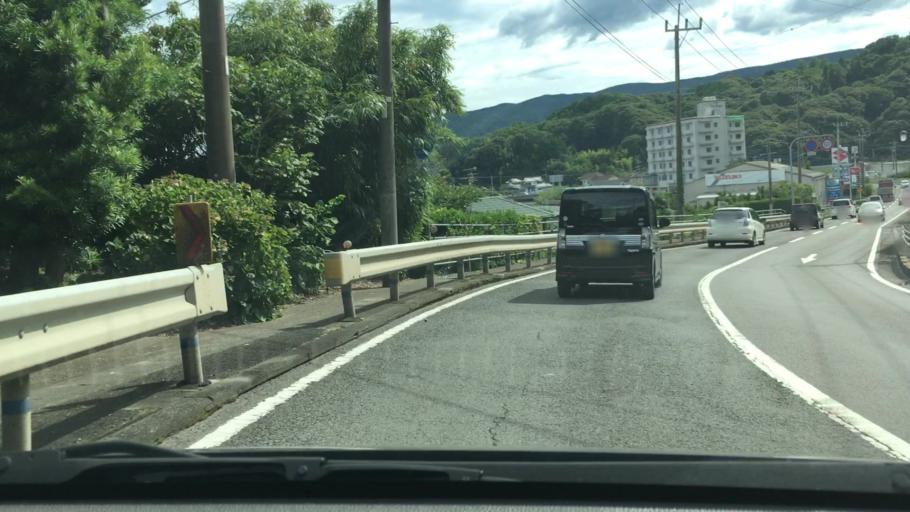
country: JP
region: Nagasaki
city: Togitsu
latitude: 32.9157
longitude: 129.7873
